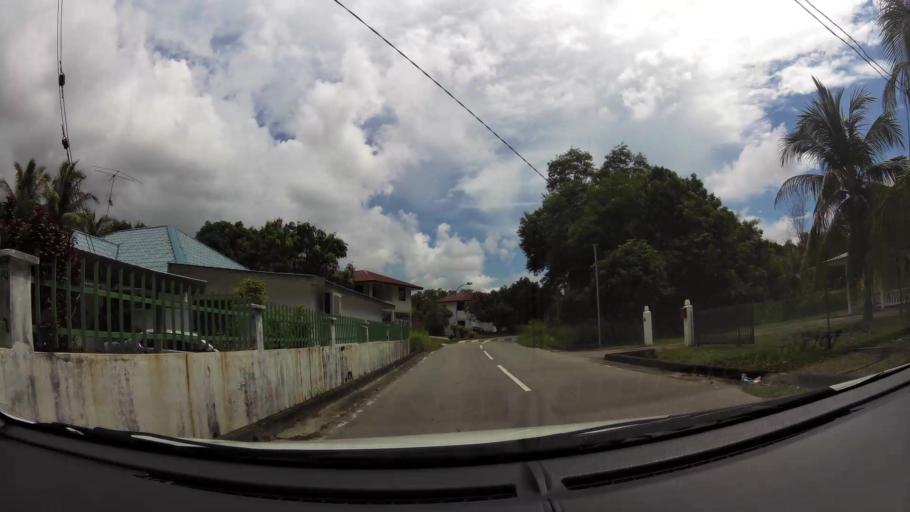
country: BN
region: Brunei and Muara
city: Bandar Seri Begawan
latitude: 4.9910
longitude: 114.9472
